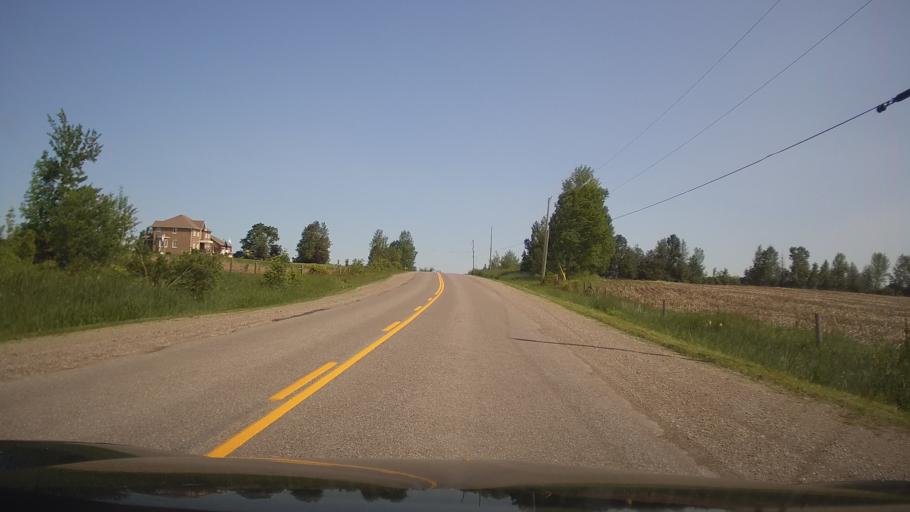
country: CA
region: Ontario
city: Omemee
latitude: 44.4539
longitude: -78.9280
